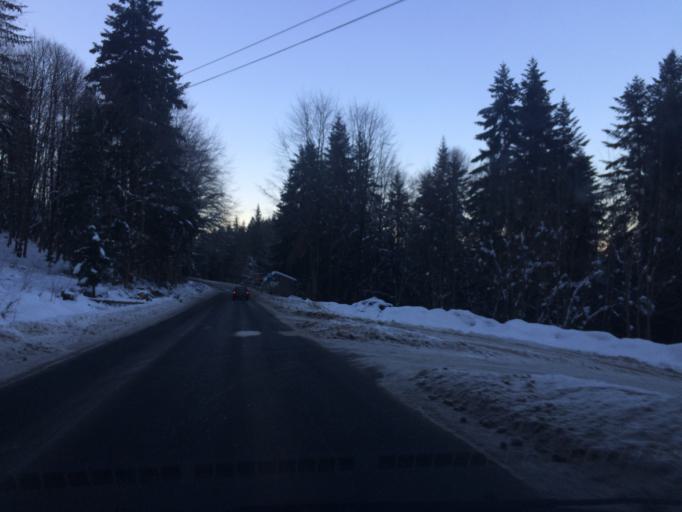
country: PL
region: Subcarpathian Voivodeship
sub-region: Powiat bieszczadzki
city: Lutowiska
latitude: 49.2895
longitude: 22.6759
